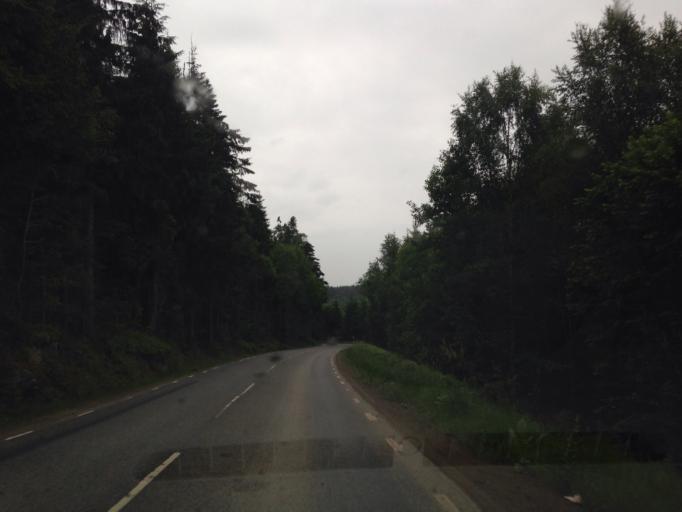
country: SE
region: Vaestra Goetaland
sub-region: Lerums Kommun
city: Lerum
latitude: 57.6867
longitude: 12.3180
